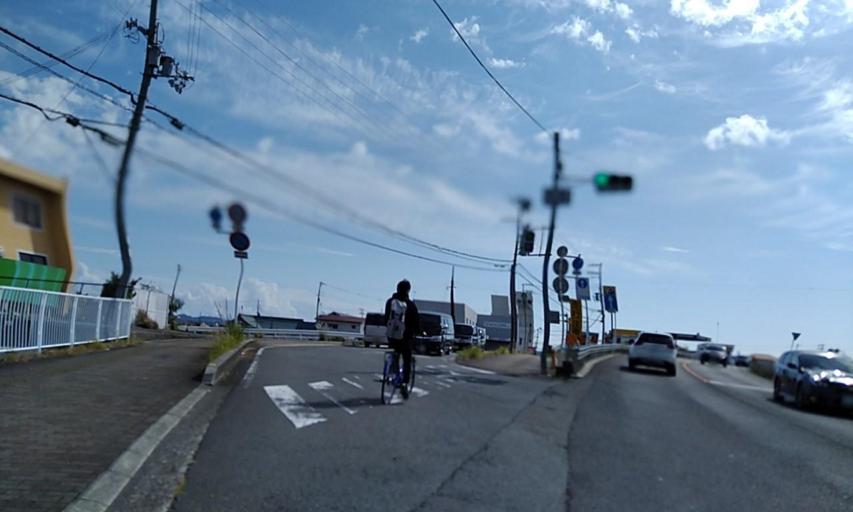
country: JP
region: Wakayama
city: Gobo
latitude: 33.9068
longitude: 135.1513
